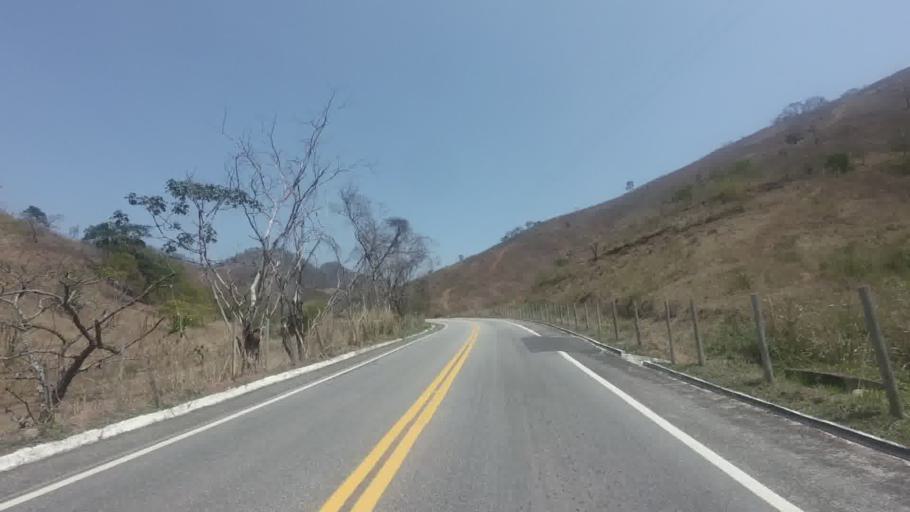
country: BR
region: Espirito Santo
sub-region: Cachoeiro De Itapemirim
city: Cachoeiro de Itapemirim
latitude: -20.8454
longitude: -41.2418
